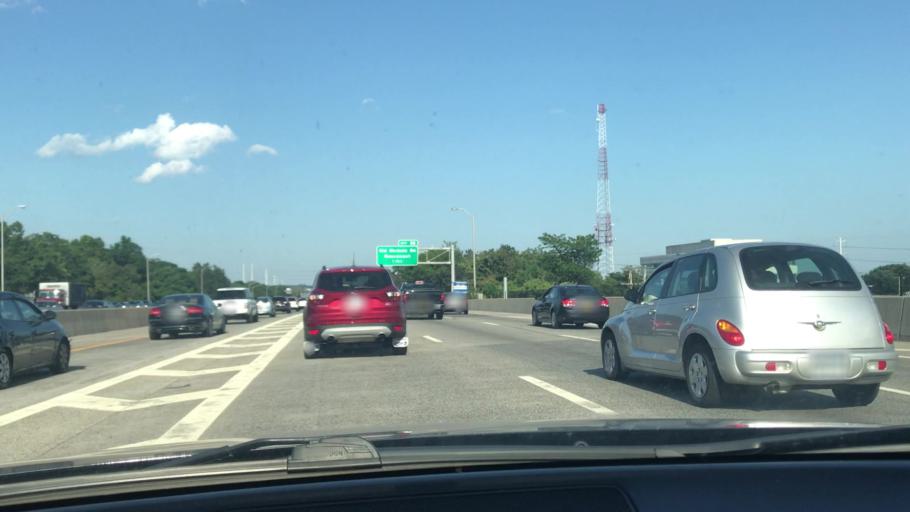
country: US
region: New York
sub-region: Suffolk County
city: Hauppauge
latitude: 40.8111
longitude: -73.1890
